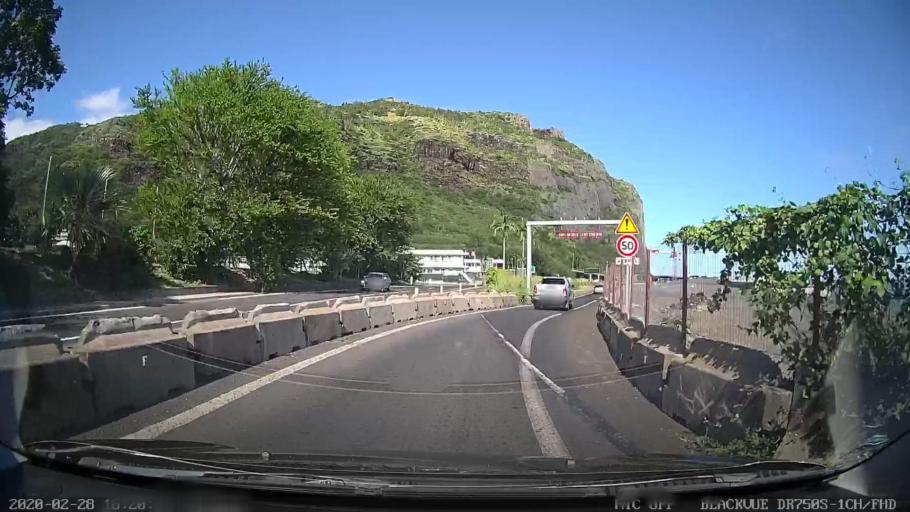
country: RE
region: Reunion
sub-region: Reunion
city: Saint-Denis
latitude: -20.8763
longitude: 55.4406
